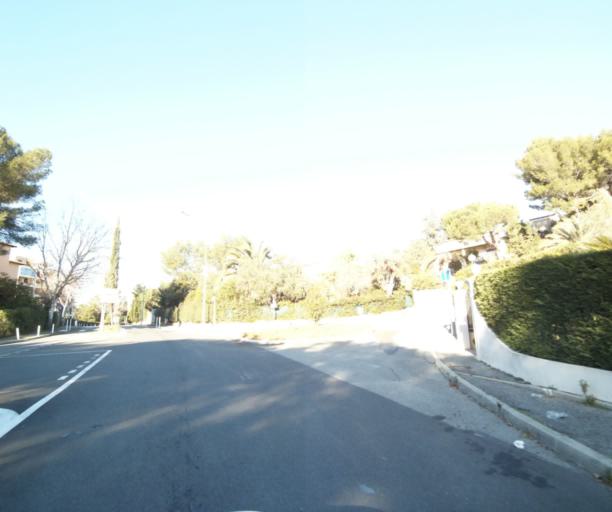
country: FR
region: Provence-Alpes-Cote d'Azur
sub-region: Departement des Alpes-Maritimes
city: Vallauris
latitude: 43.5975
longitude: 7.0705
